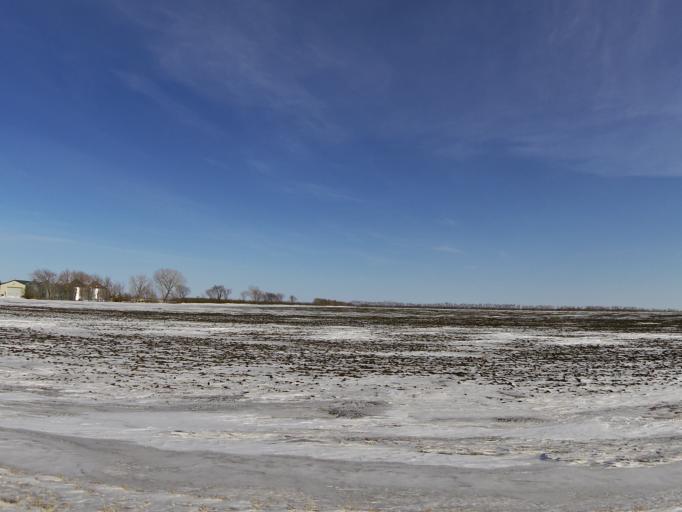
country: US
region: North Dakota
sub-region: Walsh County
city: Grafton
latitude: 48.4037
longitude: -97.2119
